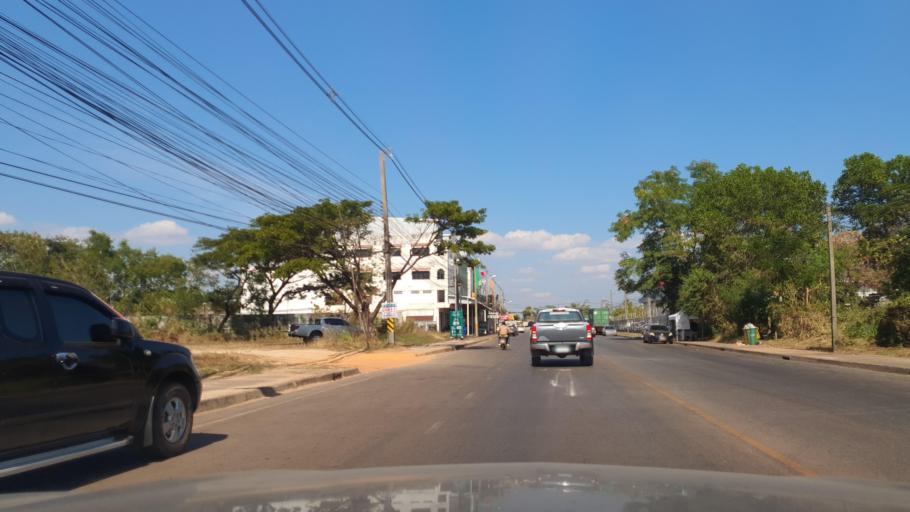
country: TH
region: Sakon Nakhon
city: Sakon Nakhon
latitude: 17.1731
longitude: 104.1270
